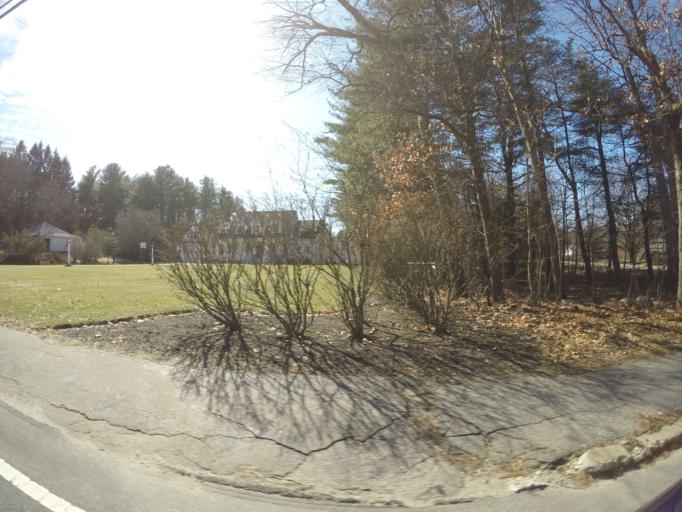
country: US
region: Massachusetts
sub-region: Bristol County
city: Easton
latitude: 42.0672
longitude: -71.1139
